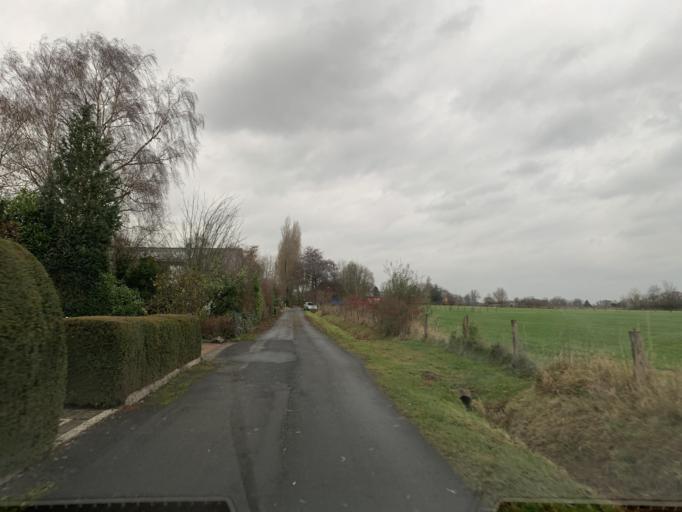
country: DE
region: North Rhine-Westphalia
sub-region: Regierungsbezirk Munster
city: Altenberge
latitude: 52.0168
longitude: 7.5044
